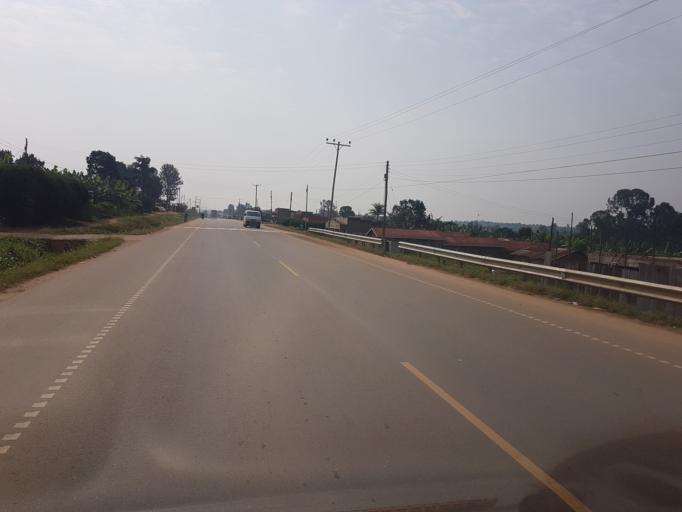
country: UG
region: Western Region
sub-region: Mbarara District
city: Bwizibwera
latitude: -0.6366
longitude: 30.6112
